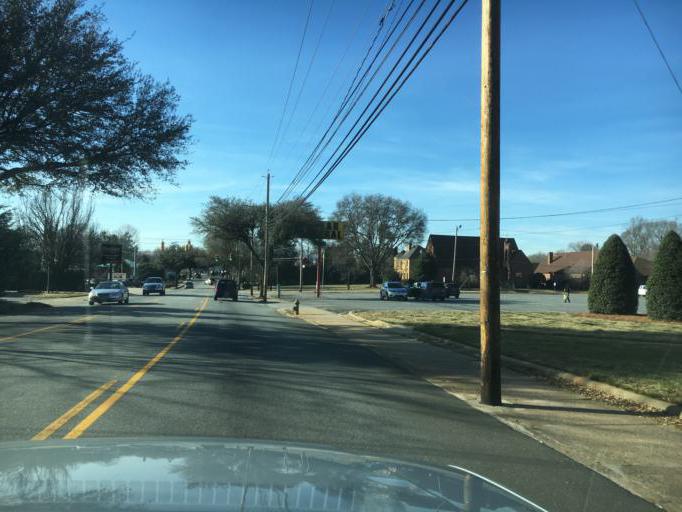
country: US
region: North Carolina
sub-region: Rutherford County
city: Forest City
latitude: 35.3383
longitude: -81.8730
